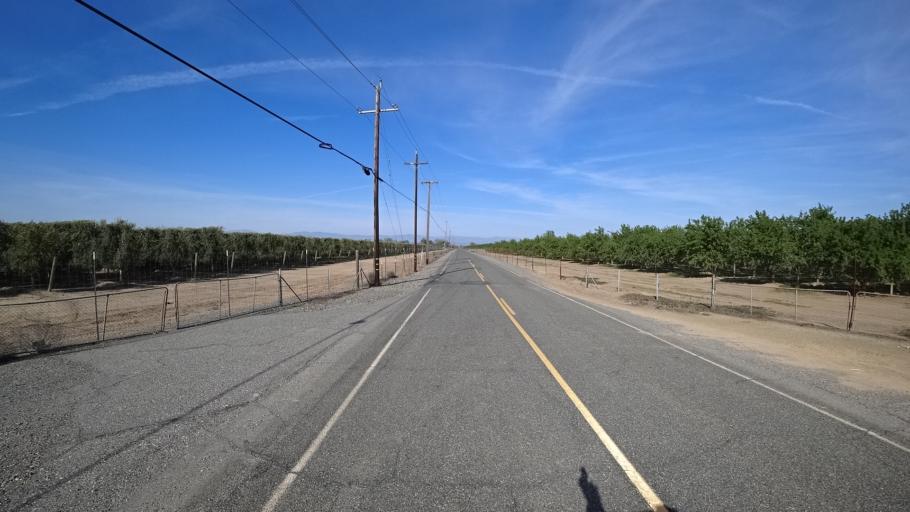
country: US
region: California
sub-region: Glenn County
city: Orland
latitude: 39.6679
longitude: -122.2074
